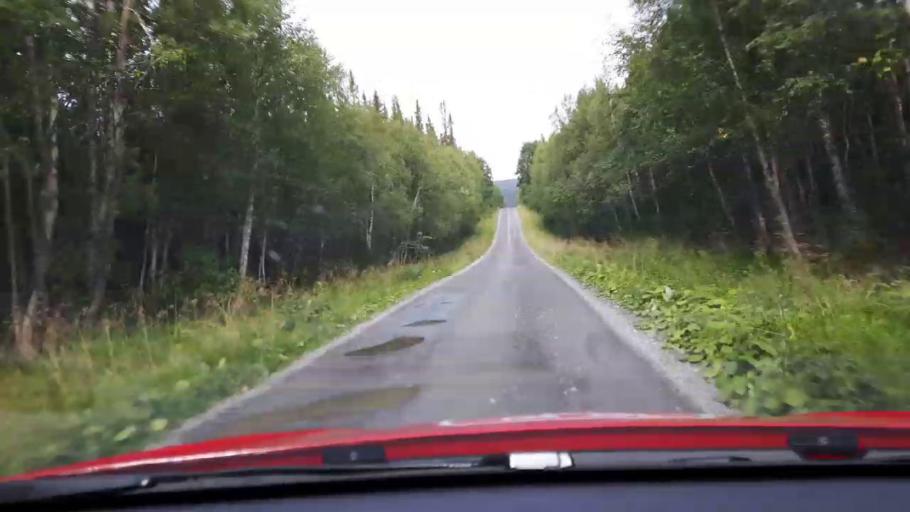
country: SE
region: Jaemtland
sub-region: Are Kommun
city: Are
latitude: 63.7952
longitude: 13.1085
